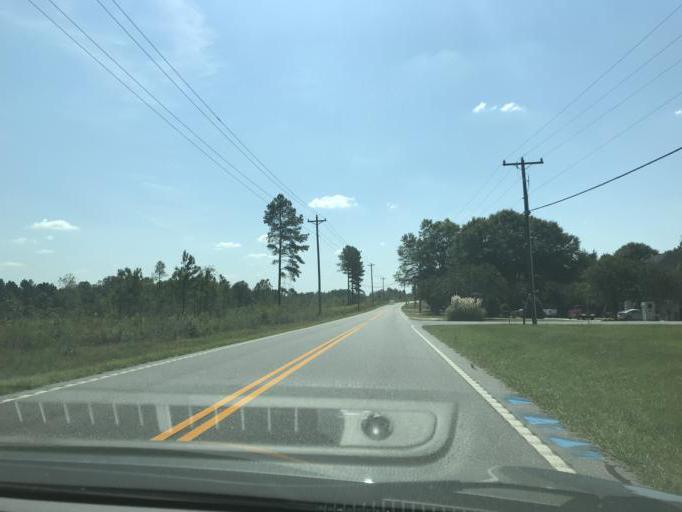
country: US
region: South Carolina
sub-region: Cherokee County
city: Gaffney
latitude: 35.1047
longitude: -81.7042
